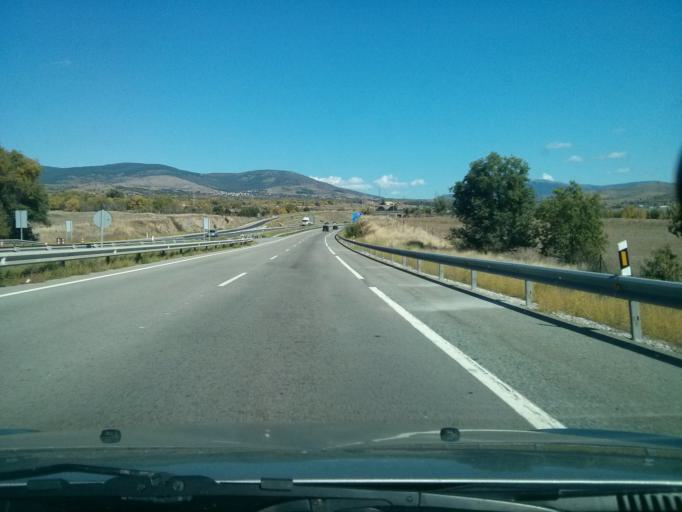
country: ES
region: Madrid
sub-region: Provincia de Madrid
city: Buitrago del Lozoya
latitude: 40.9948
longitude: -3.6419
